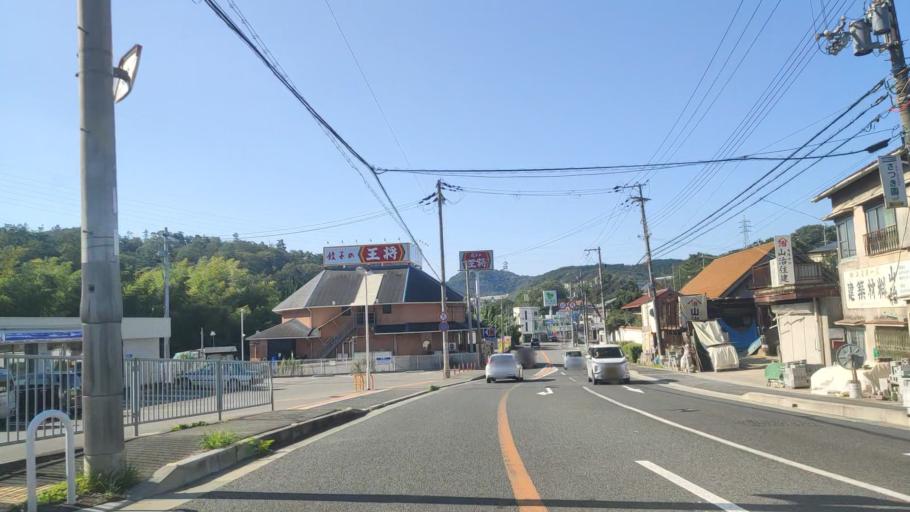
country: JP
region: Hyogo
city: Kobe
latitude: 34.7283
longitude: 135.1603
